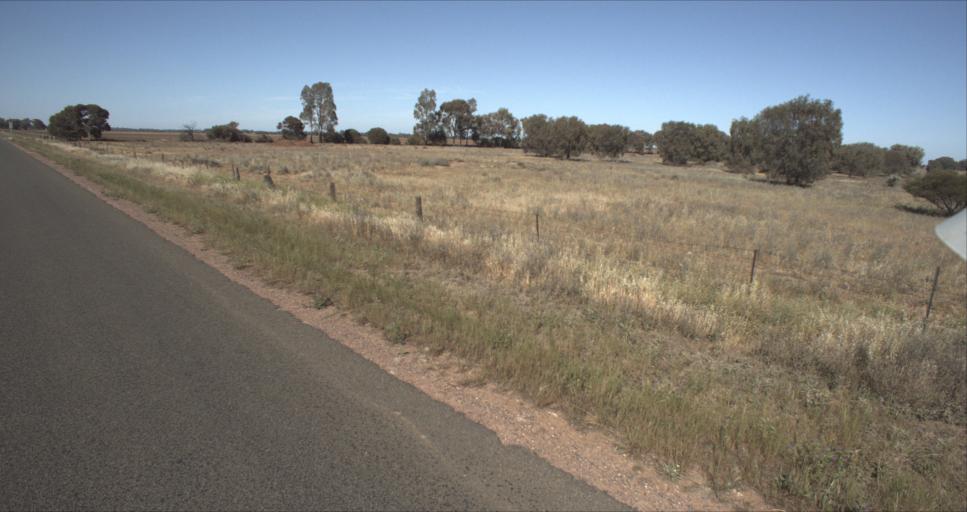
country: AU
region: New South Wales
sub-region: Leeton
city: Leeton
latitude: -34.5656
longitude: 146.2645
